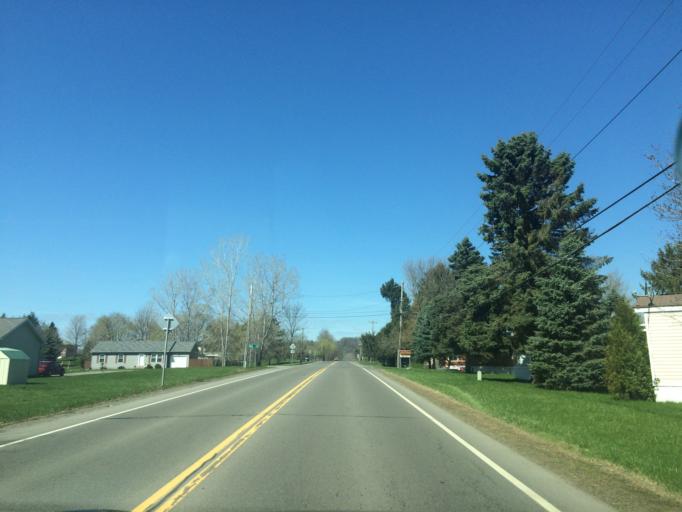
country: US
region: New York
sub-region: Wayne County
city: Macedon
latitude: 43.0942
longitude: -77.3493
